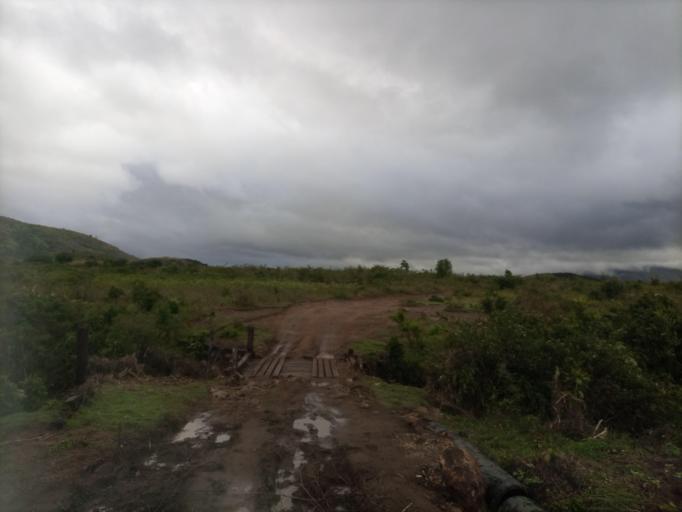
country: MG
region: Anosy
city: Fort Dauphin
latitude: -24.7606
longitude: 47.0676
